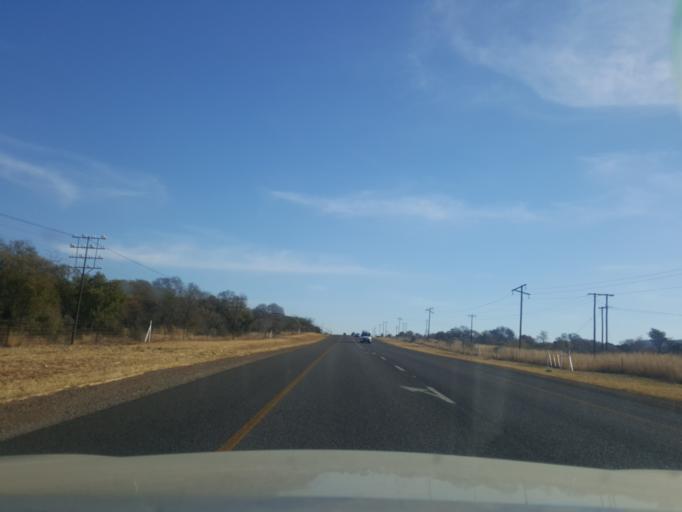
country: ZA
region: North-West
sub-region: Ngaka Modiri Molema District Municipality
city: Zeerust
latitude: -25.5236
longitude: 26.1557
